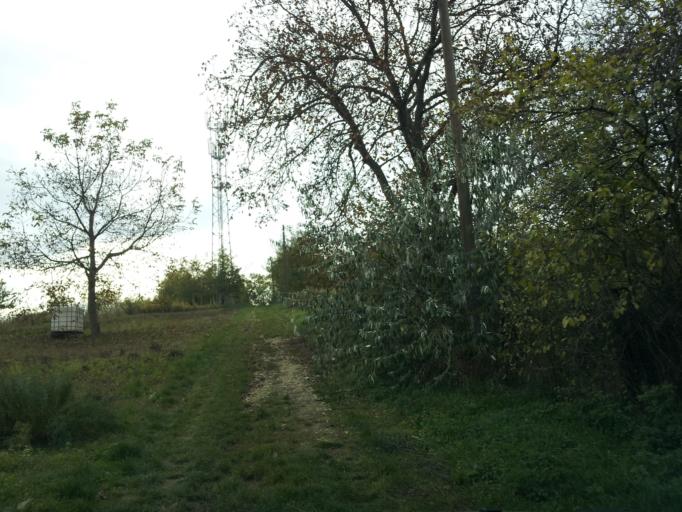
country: HU
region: Gyor-Moson-Sopron
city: Pannonhalma
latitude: 47.4896
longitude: 17.6973
